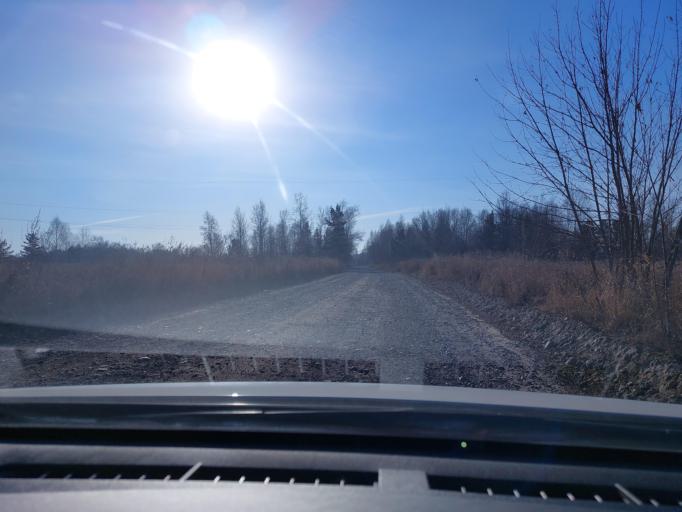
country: RU
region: Irkutsk
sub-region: Irkutskiy Rayon
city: Irkutsk
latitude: 52.3034
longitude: 104.2764
